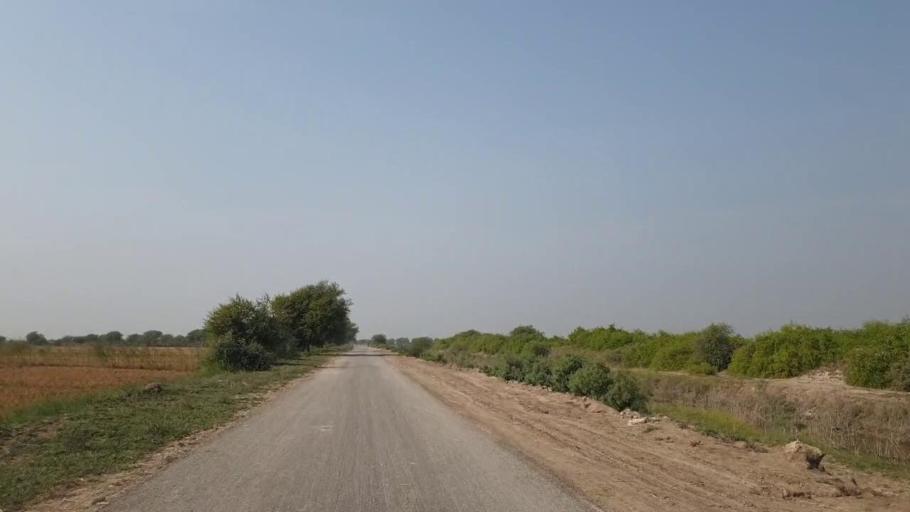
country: PK
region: Sindh
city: Matli
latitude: 24.9582
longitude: 68.5232
